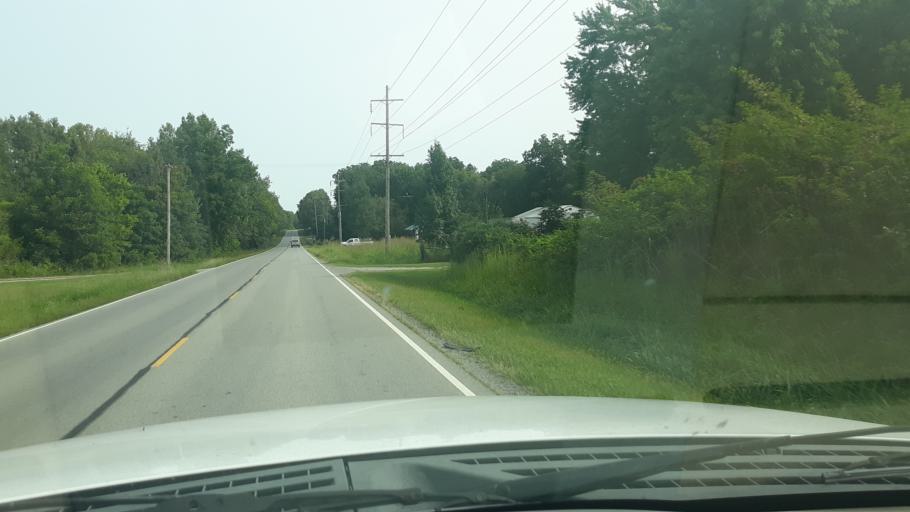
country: US
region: Illinois
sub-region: White County
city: Norris City
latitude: 37.9557
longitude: -88.3369
